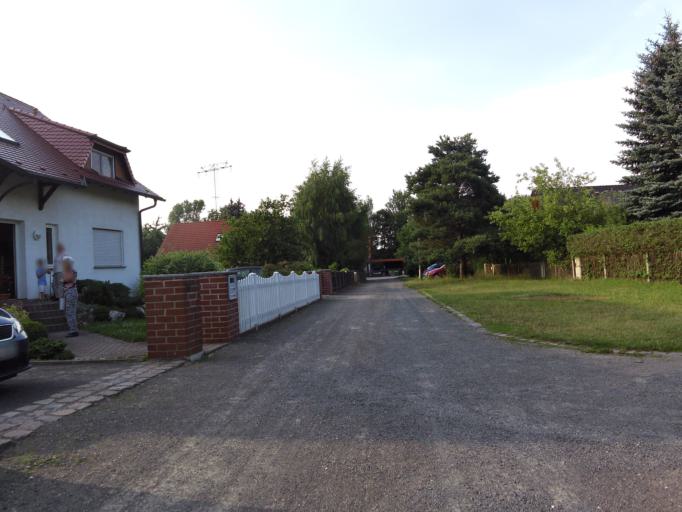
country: DE
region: Saxony
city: Leipzig
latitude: 51.3635
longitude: 12.4239
